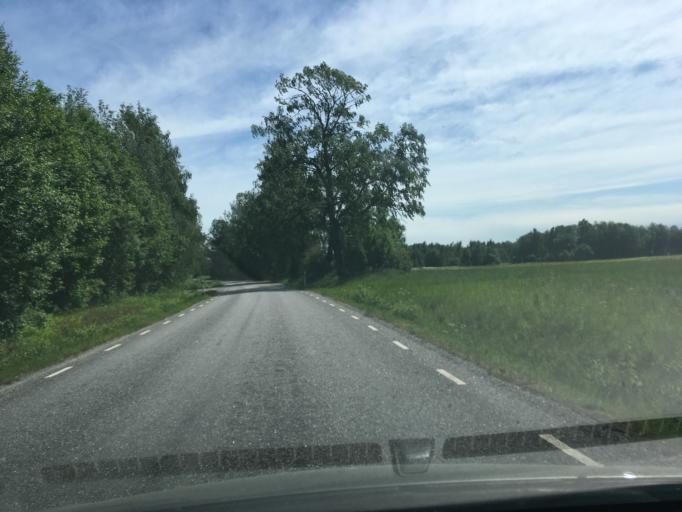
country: EE
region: Paernumaa
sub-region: Audru vald
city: Audru
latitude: 58.4255
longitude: 24.4313
